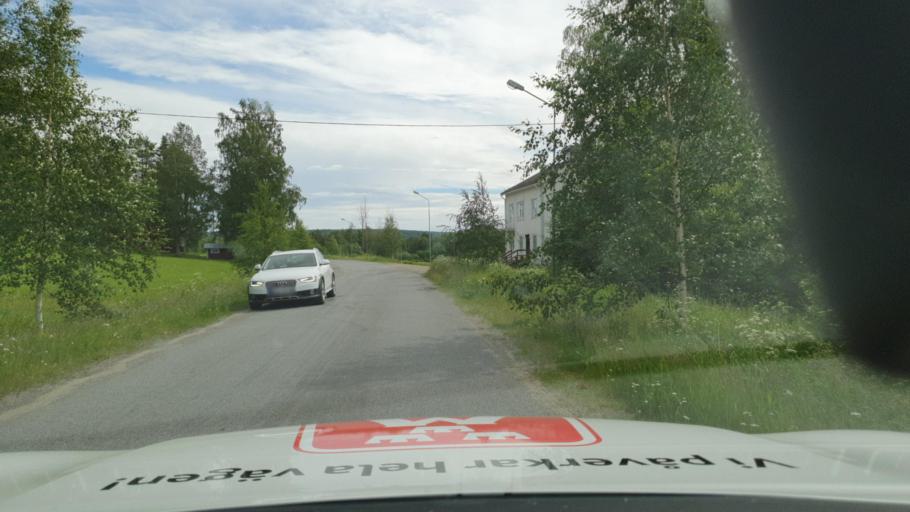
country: SE
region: Vaesterbotten
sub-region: Skelleftea Kommun
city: Burtraesk
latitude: 64.4866
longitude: 20.5065
